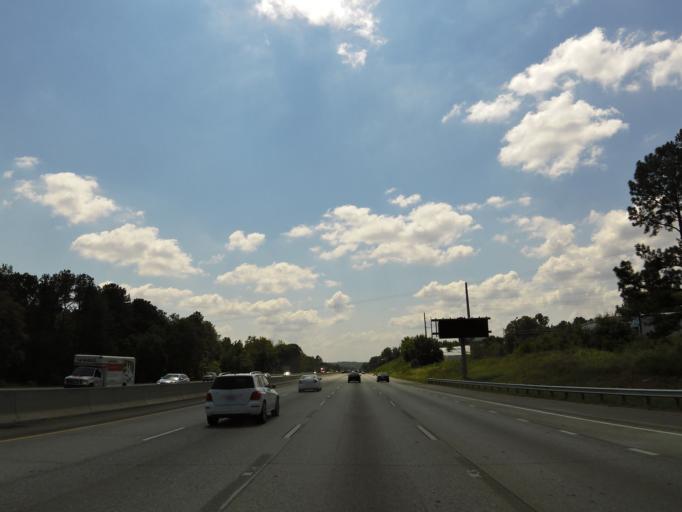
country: US
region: North Carolina
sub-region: Cabarrus County
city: Harrisburg
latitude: 35.3956
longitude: -80.7011
